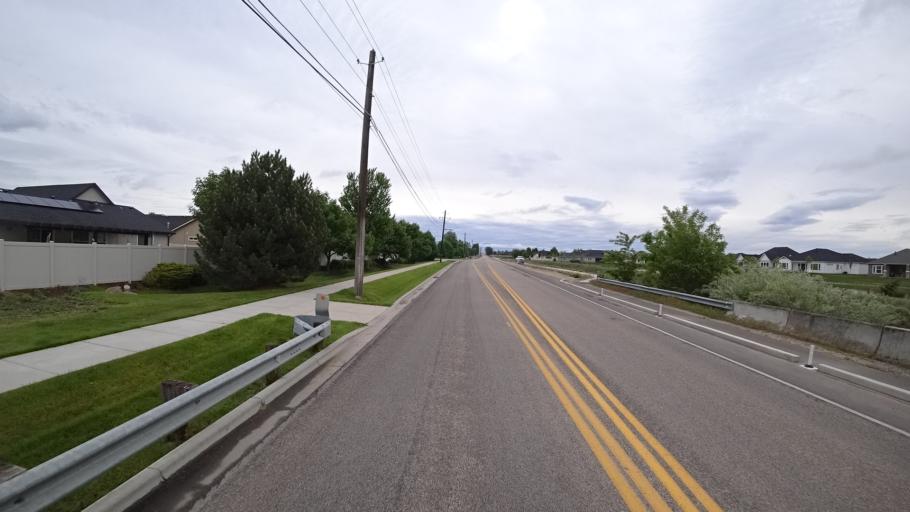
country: US
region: Idaho
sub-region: Ada County
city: Star
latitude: 43.7065
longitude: -116.4815
